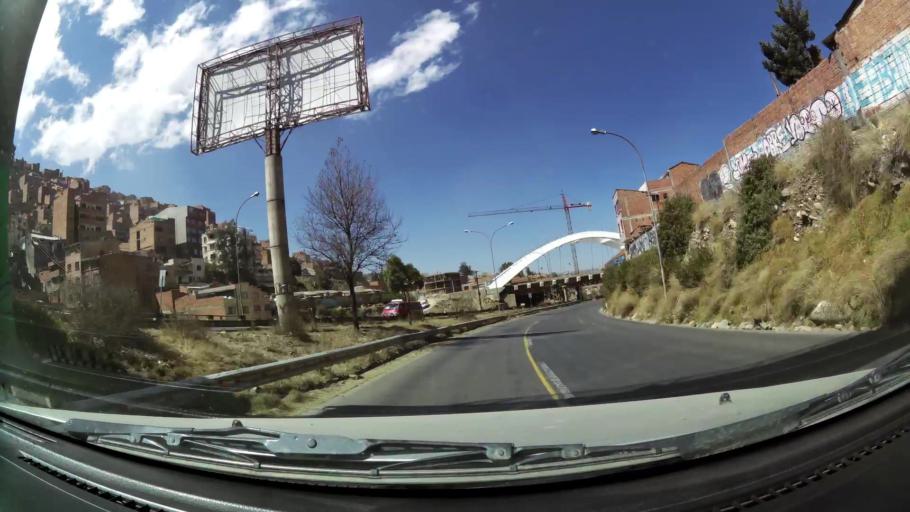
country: BO
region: La Paz
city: La Paz
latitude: -16.4807
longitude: -68.1487
